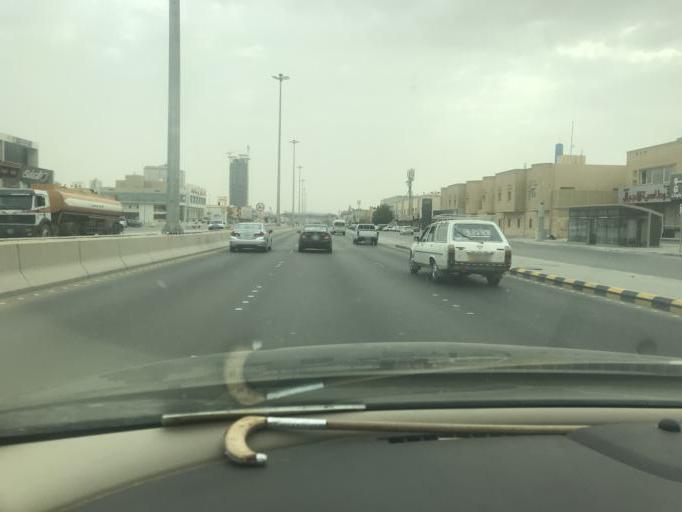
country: SA
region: Ar Riyad
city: Riyadh
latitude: 24.8158
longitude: 46.6356
